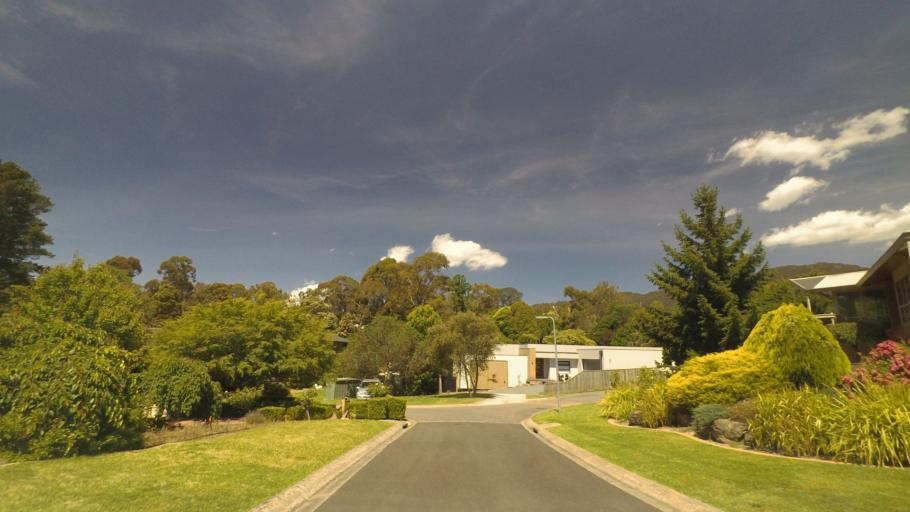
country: AU
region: Victoria
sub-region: Yarra Ranges
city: Montrose
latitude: -37.8077
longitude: 145.3370
